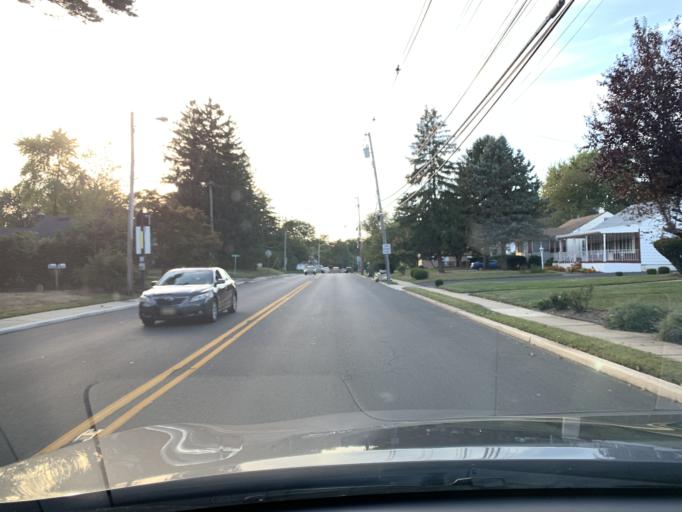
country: US
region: New Jersey
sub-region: Monmouth County
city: Eatontown
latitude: 40.3052
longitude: -74.0457
